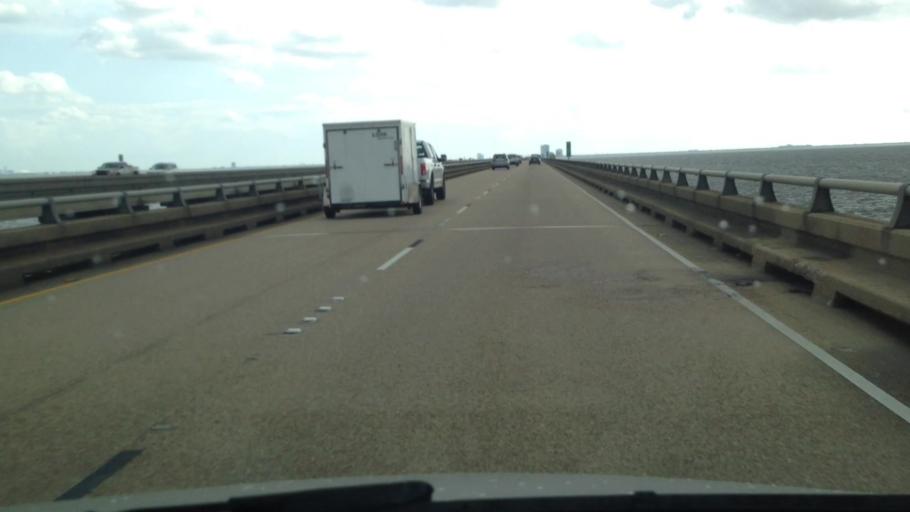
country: US
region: Louisiana
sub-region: Jefferson Parish
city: Metairie
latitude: 30.0972
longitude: -90.1410
